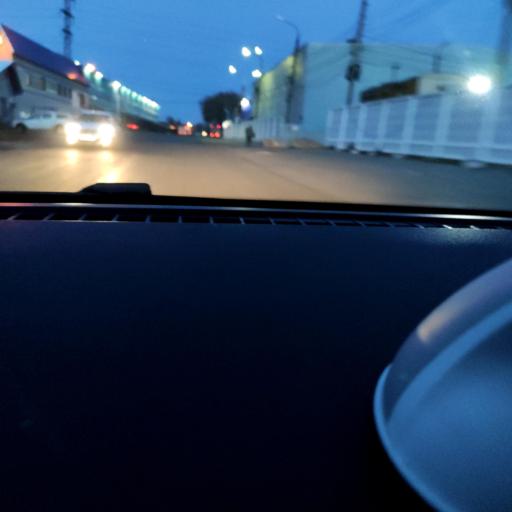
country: RU
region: Samara
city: Samara
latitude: 53.1822
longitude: 50.1726
